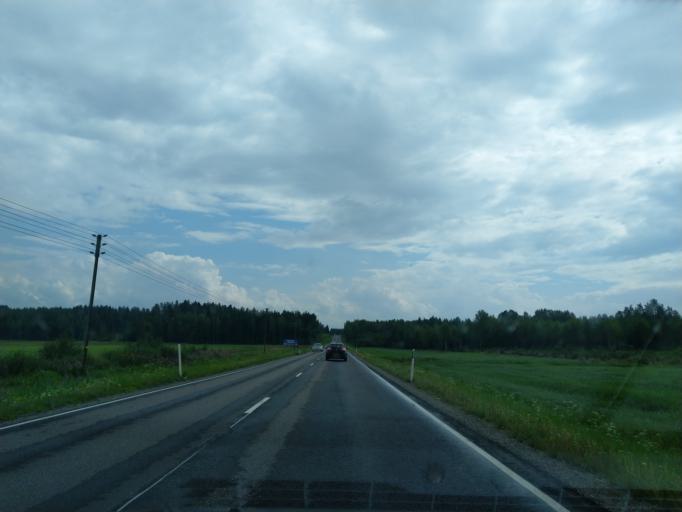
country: FI
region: South Karelia
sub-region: Imatra
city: Parikkala
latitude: 61.6227
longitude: 29.4392
